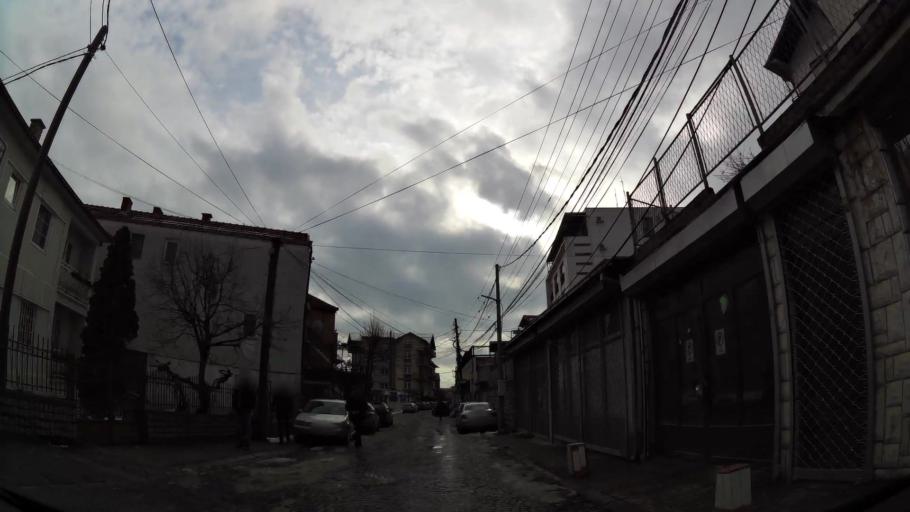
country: XK
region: Pristina
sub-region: Komuna e Prishtines
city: Pristina
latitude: 42.6645
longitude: 21.1518
